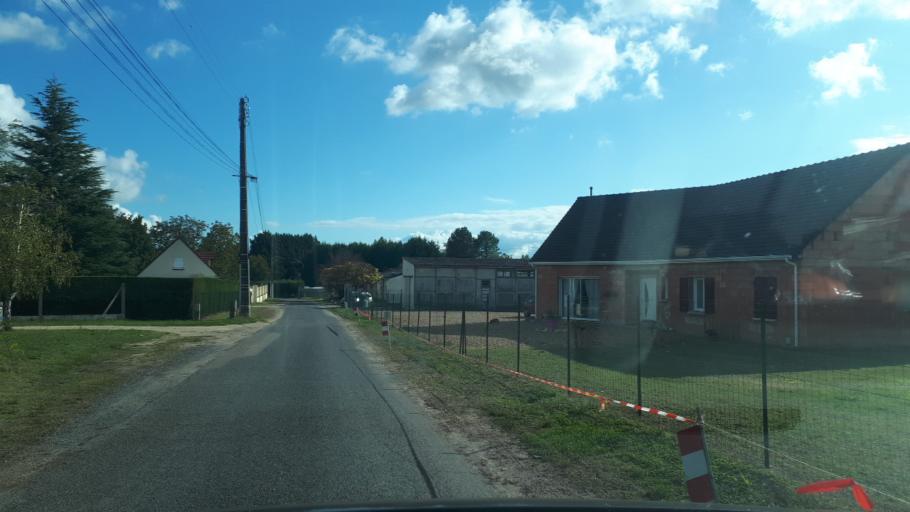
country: FR
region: Centre
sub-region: Departement du Loir-et-Cher
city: Thesee
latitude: 47.3212
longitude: 1.3197
